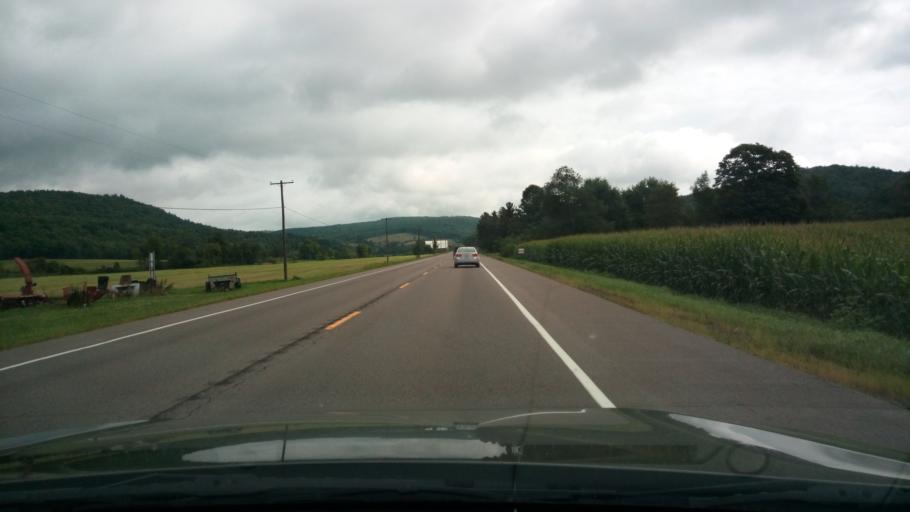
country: US
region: New York
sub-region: Schuyler County
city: Montour Falls
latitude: 42.3117
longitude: -76.6702
